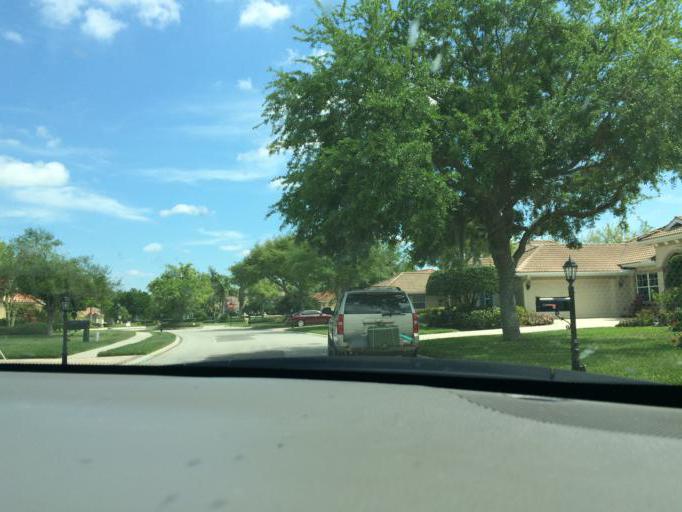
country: US
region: Florida
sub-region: Manatee County
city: Ellenton
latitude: 27.5107
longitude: -82.4423
